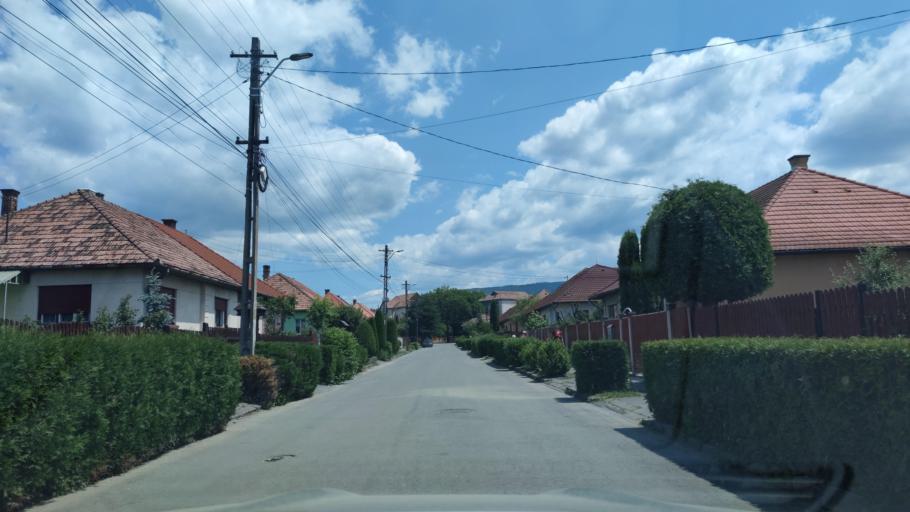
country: RO
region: Harghita
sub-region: Municipiul Gheorgheni
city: Gheorgheni
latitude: 46.7256
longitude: 25.5995
